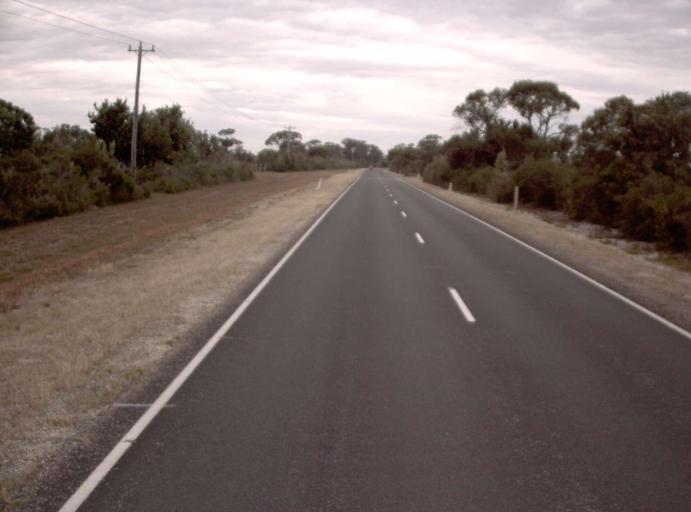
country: AU
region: Victoria
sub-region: Wellington
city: Sale
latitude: -38.1880
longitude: 147.3699
